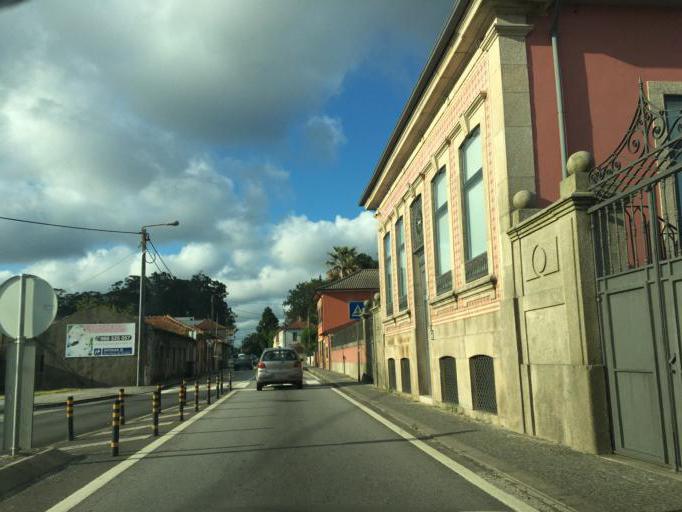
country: PT
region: Porto
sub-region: Maia
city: Anta
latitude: 41.2715
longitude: -8.6098
